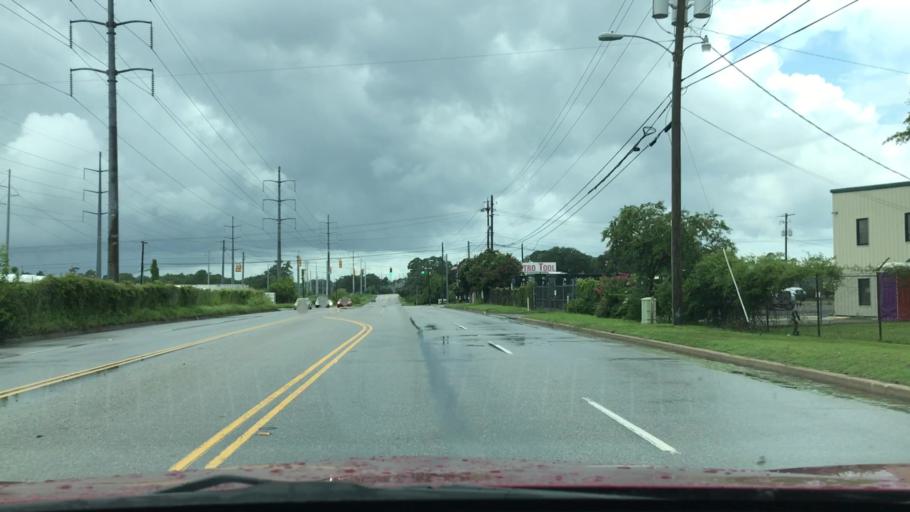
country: US
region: South Carolina
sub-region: Charleston County
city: North Charleston
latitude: 32.8473
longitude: -80.0035
